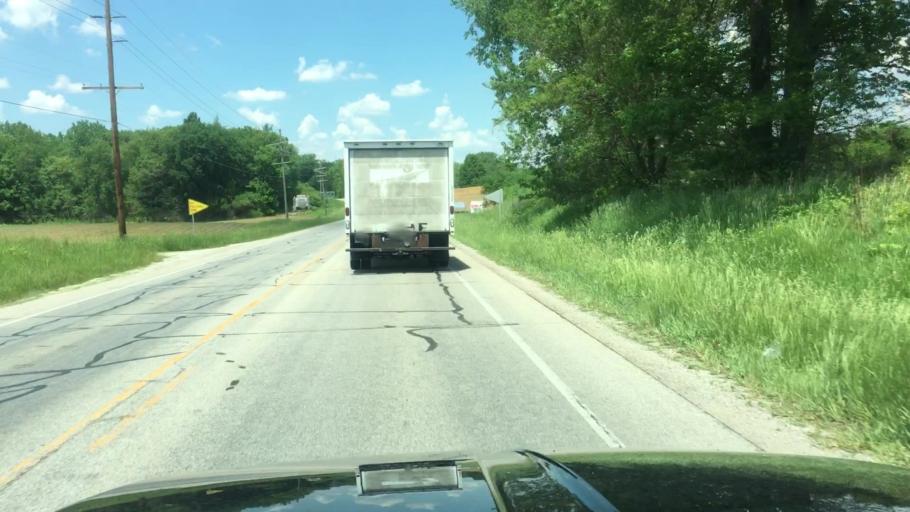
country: US
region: Indiana
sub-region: Kosciusko County
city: North Webster
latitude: 41.3118
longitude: -85.6911
